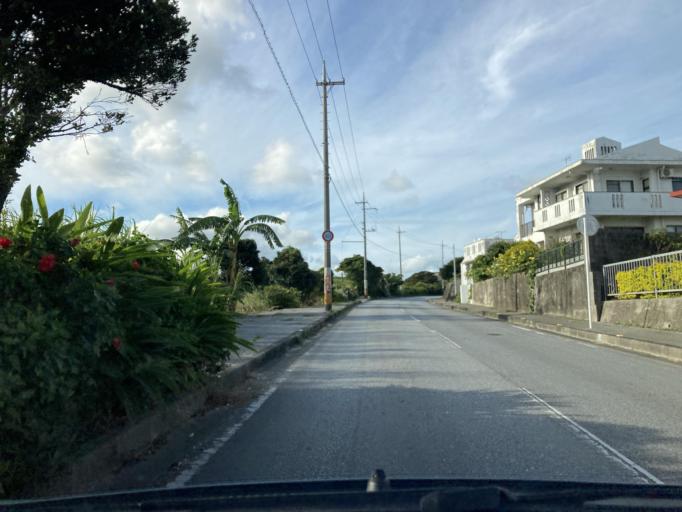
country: JP
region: Okinawa
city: Tomigusuku
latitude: 26.1442
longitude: 127.7459
